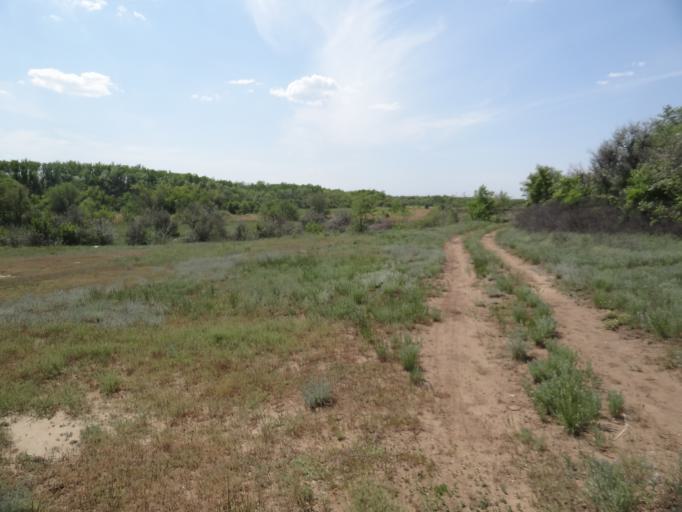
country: RU
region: Saratov
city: Privolzhskiy
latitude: 51.3471
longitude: 46.1559
